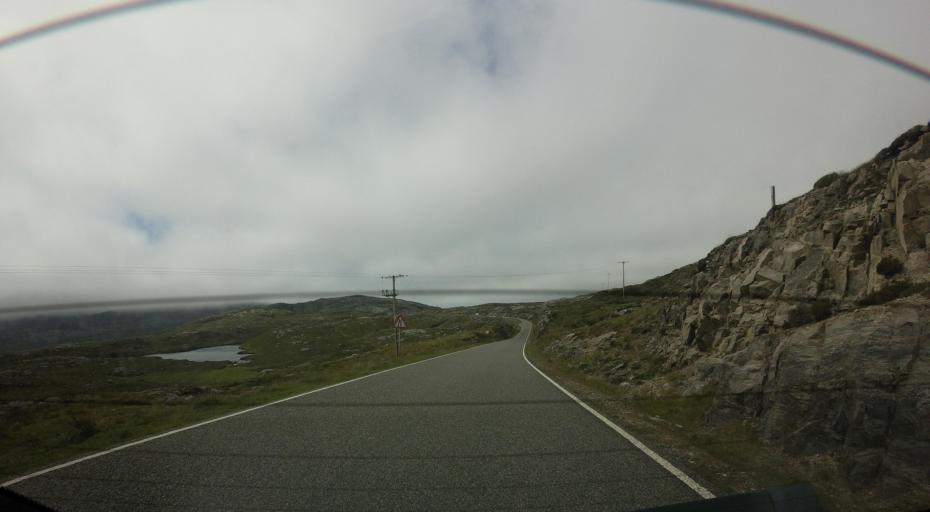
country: GB
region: Scotland
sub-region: Eilean Siar
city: Harris
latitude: 57.8472
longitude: -6.8324
